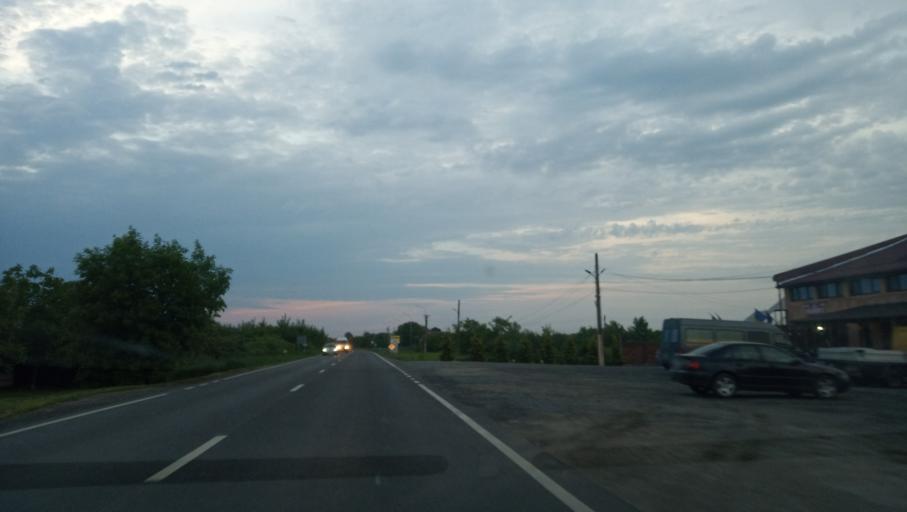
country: RO
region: Timis
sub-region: Comuna Jebel
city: Jebel
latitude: 45.5504
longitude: 21.2229
